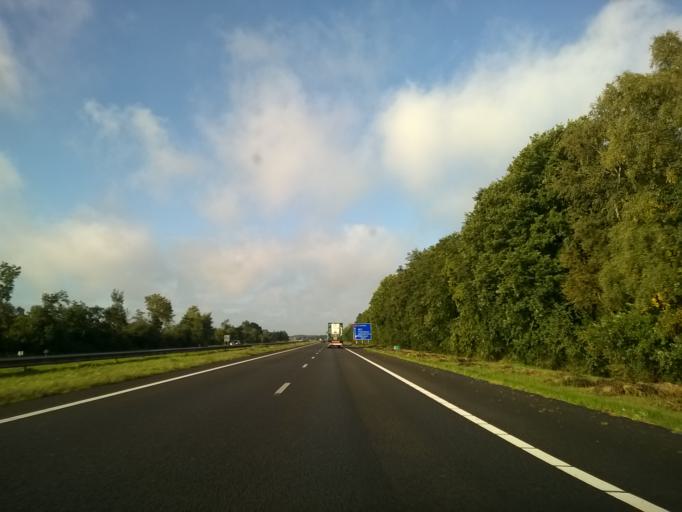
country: NL
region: Friesland
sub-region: Gemeente Achtkarspelen
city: Surhuisterveen
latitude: 53.1357
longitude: 6.2046
